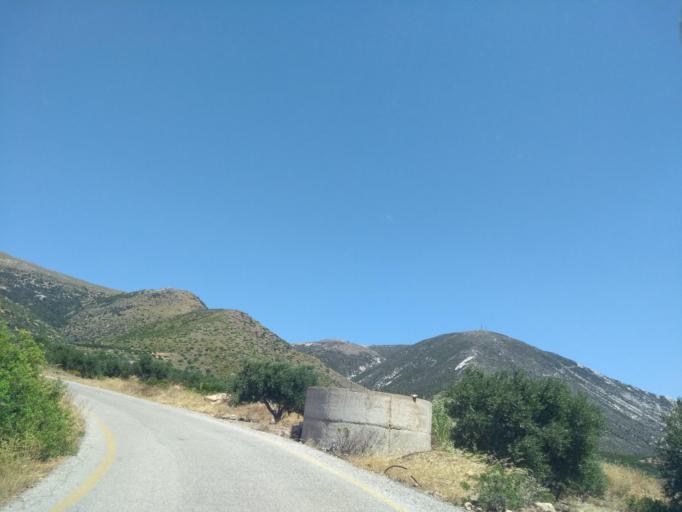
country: GR
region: Crete
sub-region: Nomos Chanias
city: Vryses
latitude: 35.3579
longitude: 23.5435
